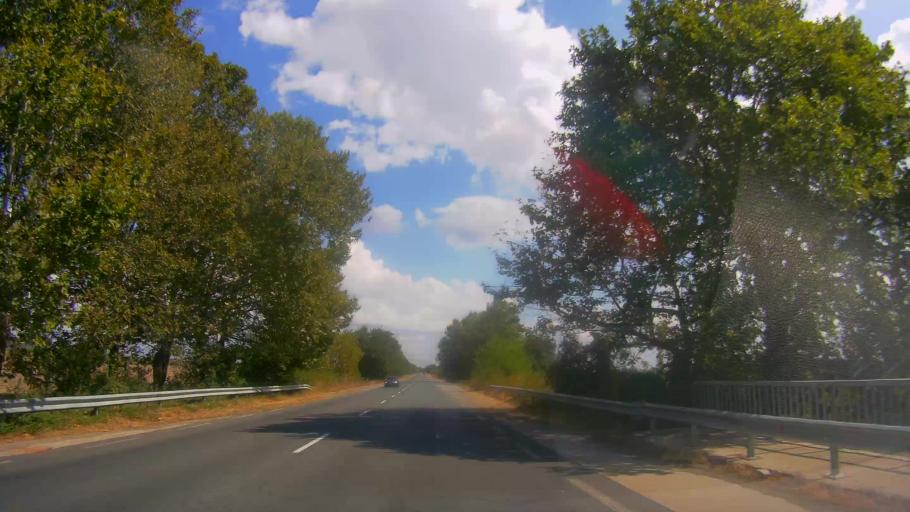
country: BG
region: Sliven
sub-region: Obshtina Sliven
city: Kermen
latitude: 42.6348
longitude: 26.1601
